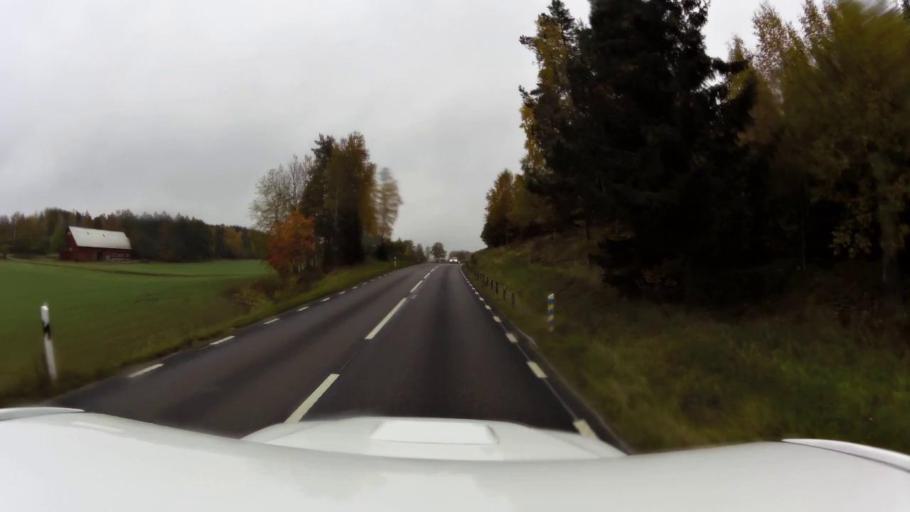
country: SE
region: OEstergoetland
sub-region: Linkopings Kommun
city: Linghem
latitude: 58.3606
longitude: 15.8272
